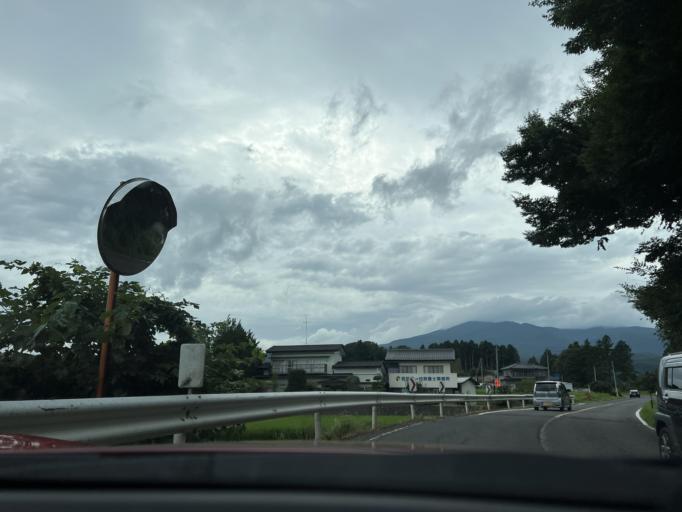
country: JP
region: Fukushima
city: Motomiya
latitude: 37.5516
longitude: 140.3618
